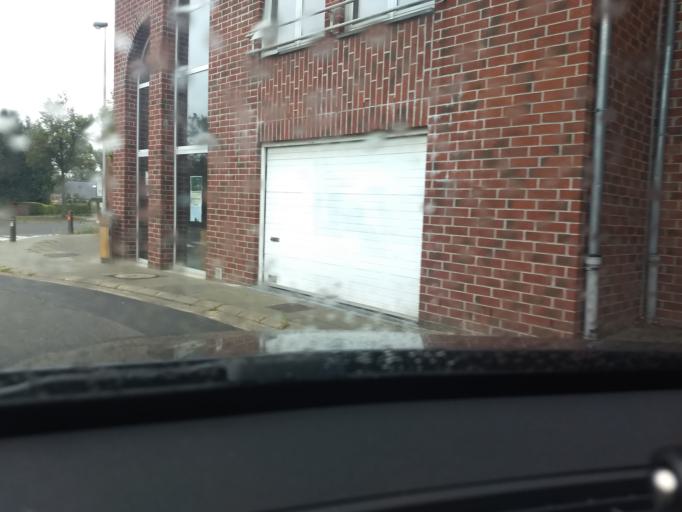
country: BE
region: Wallonia
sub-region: Province du Brabant Wallon
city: Braine-l'Alleud
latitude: 50.6783
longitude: 4.3708
